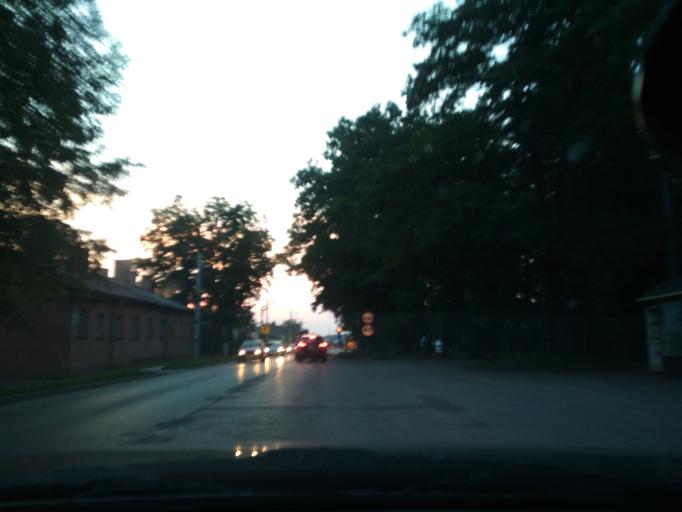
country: PL
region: Silesian Voivodeship
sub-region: Powiat zawiercianski
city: Ogrodzieniec
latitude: 50.4622
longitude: 19.4950
